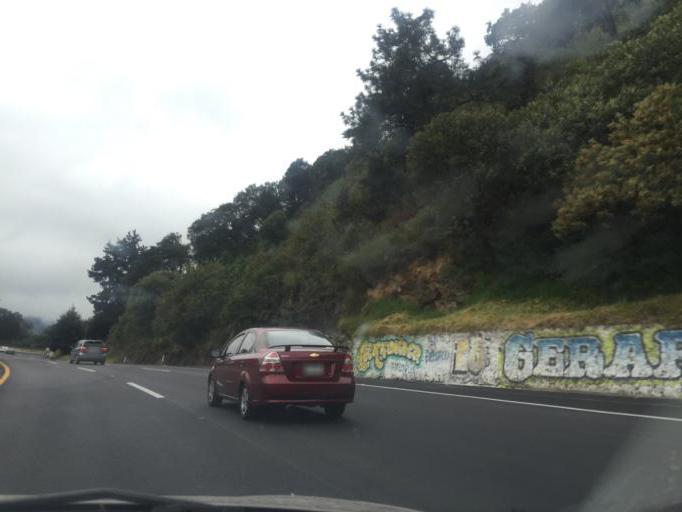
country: MX
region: Mexico City
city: Xochimilco
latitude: 19.2110
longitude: -99.1345
